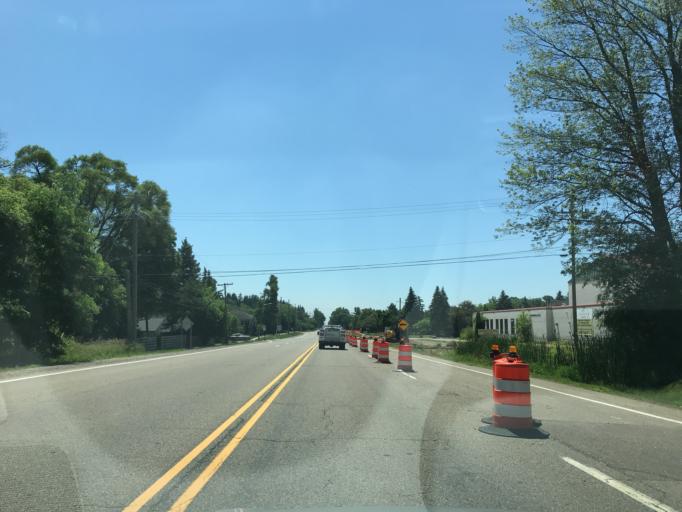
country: US
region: Michigan
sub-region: Oakland County
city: Franklin
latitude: 42.5063
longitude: -83.3395
